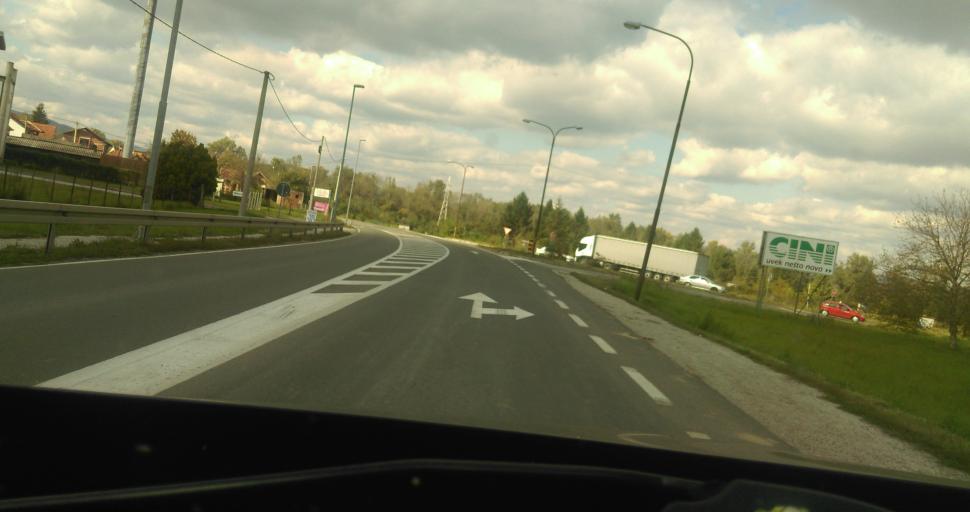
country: RS
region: Central Serbia
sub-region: Moravicki Okrug
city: Cacak
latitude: 43.8894
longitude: 20.3143
